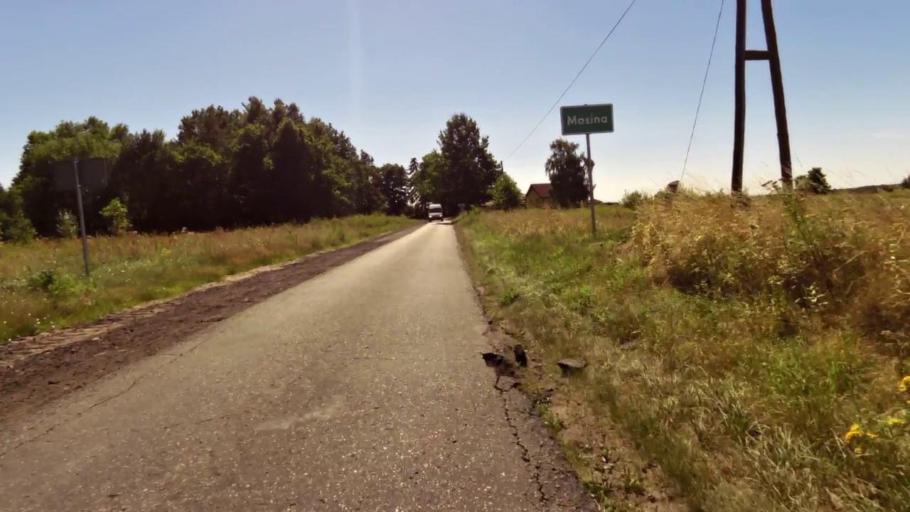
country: PL
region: West Pomeranian Voivodeship
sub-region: Powiat szczecinecki
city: Szczecinek
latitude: 53.6895
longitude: 16.6053
